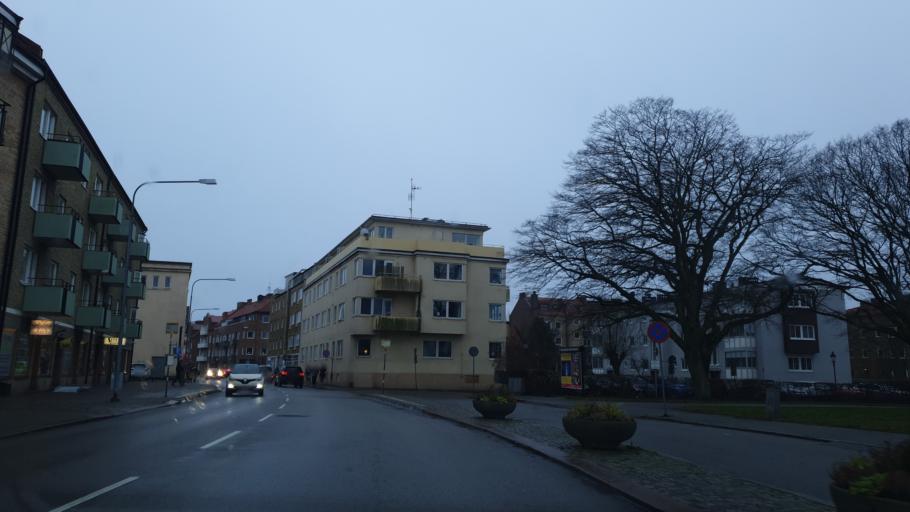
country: SE
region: Skane
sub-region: Trelleborgs Kommun
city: Trelleborg
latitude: 55.3757
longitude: 13.1532
